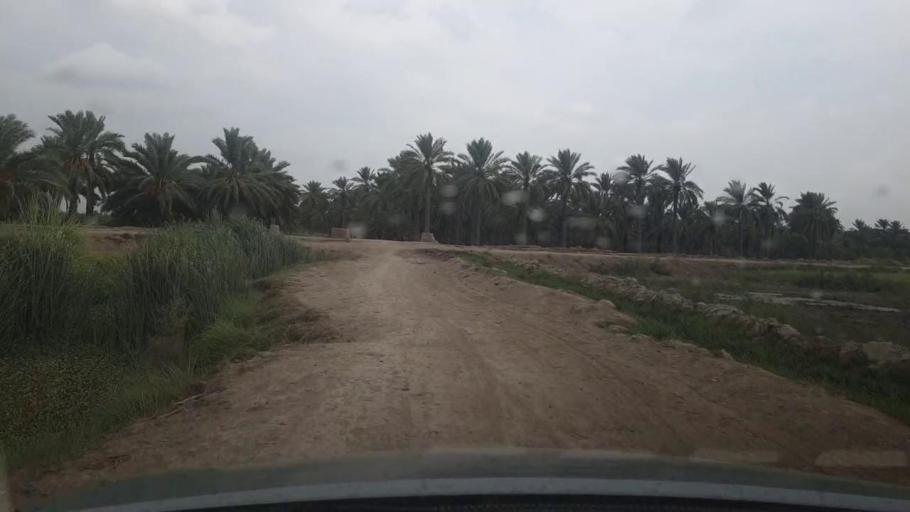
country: PK
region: Sindh
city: Khairpur
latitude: 27.5550
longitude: 68.6941
